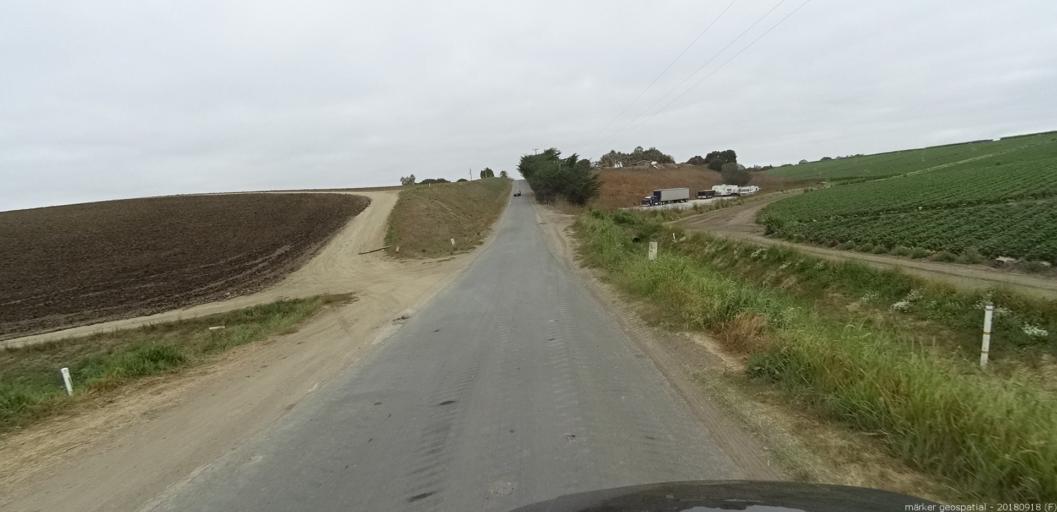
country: US
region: California
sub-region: Monterey County
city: Boronda
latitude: 36.7351
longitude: -121.7009
